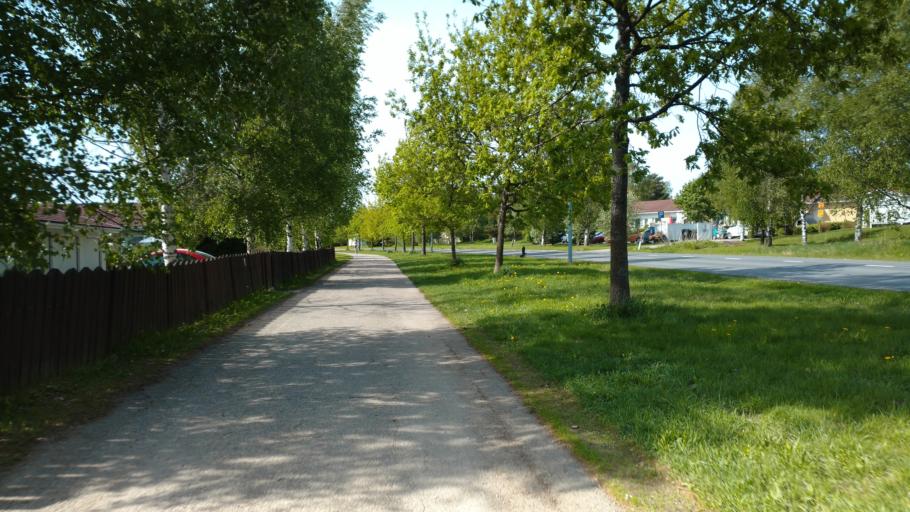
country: FI
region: Varsinais-Suomi
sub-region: Salo
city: Salo
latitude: 60.3774
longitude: 23.1614
